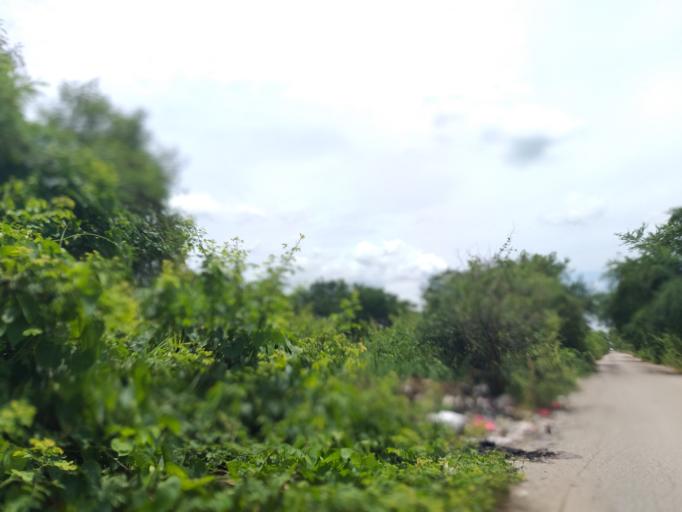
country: TH
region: Pathum Thani
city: Ban Lam Luk Ka
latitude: 13.9861
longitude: 100.8461
